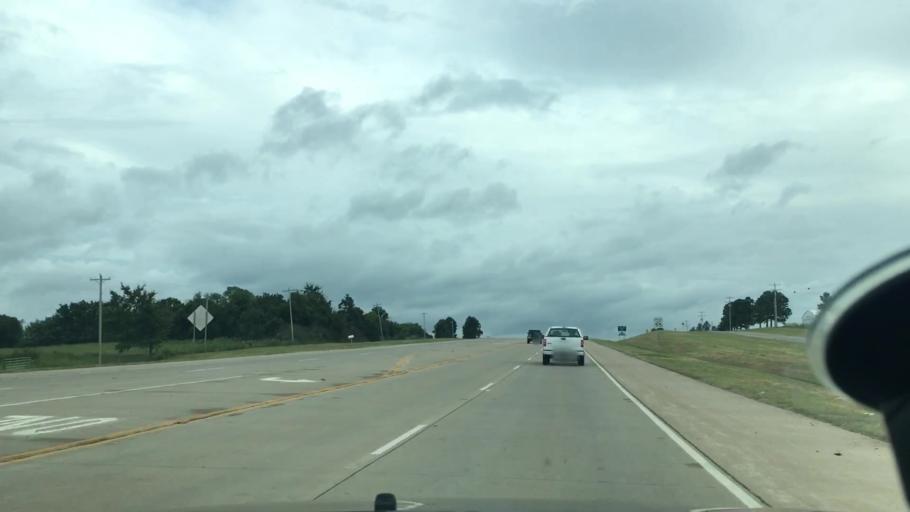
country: US
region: Oklahoma
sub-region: Seminole County
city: Seminole
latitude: 35.2754
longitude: -96.6706
